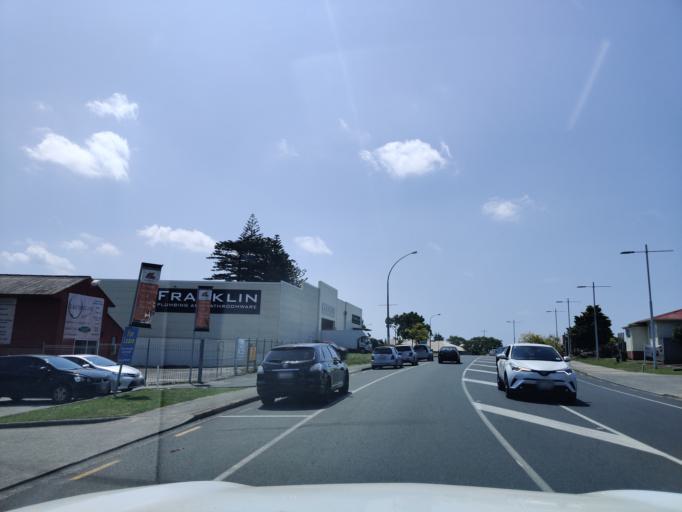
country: NZ
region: Auckland
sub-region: Auckland
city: Pukekohe East
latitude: -37.2001
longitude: 174.9080
